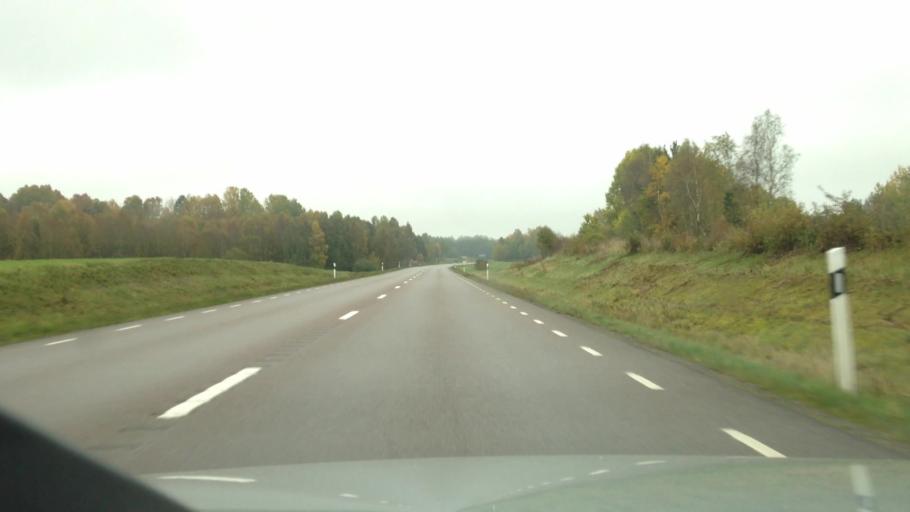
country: SE
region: Vaestra Goetaland
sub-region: Falkopings Kommun
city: Falkoeping
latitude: 58.2535
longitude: 13.5072
